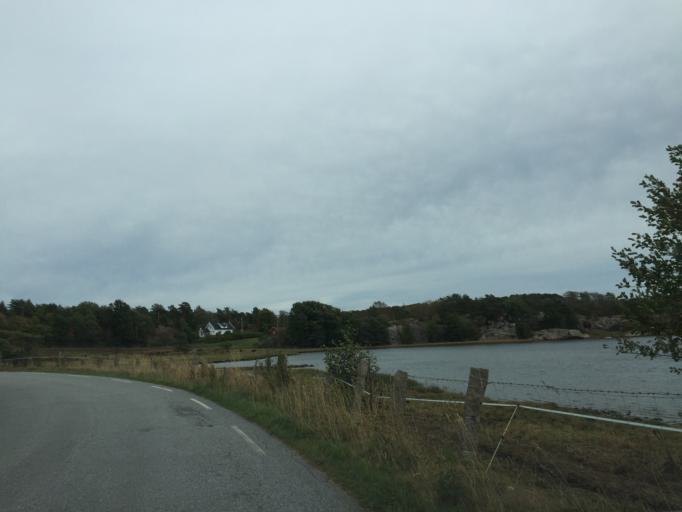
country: NO
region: Ostfold
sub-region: Hvaler
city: Skjaerhalden
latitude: 59.0463
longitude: 11.0403
